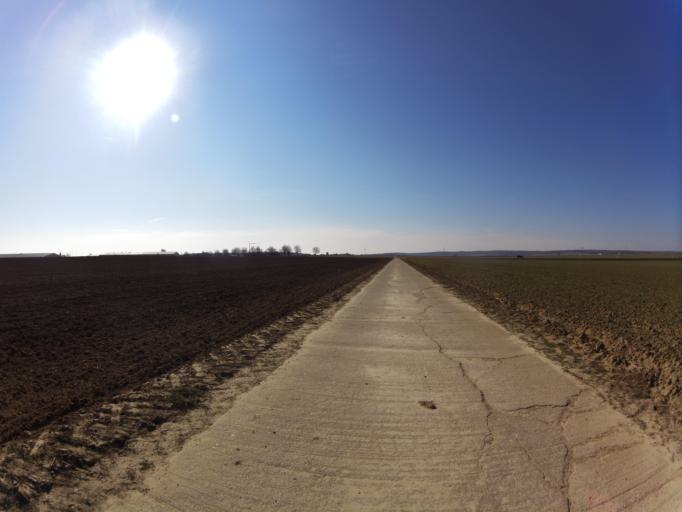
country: DE
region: Bavaria
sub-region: Regierungsbezirk Unterfranken
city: Unterpleichfeld
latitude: 49.8746
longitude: 10.0541
